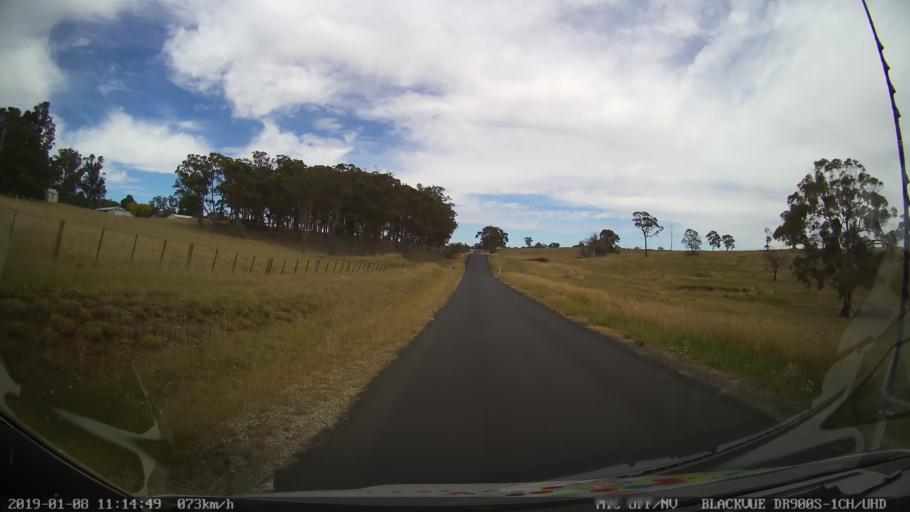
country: AU
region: New South Wales
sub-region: Guyra
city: Guyra
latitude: -30.2246
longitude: 151.5849
